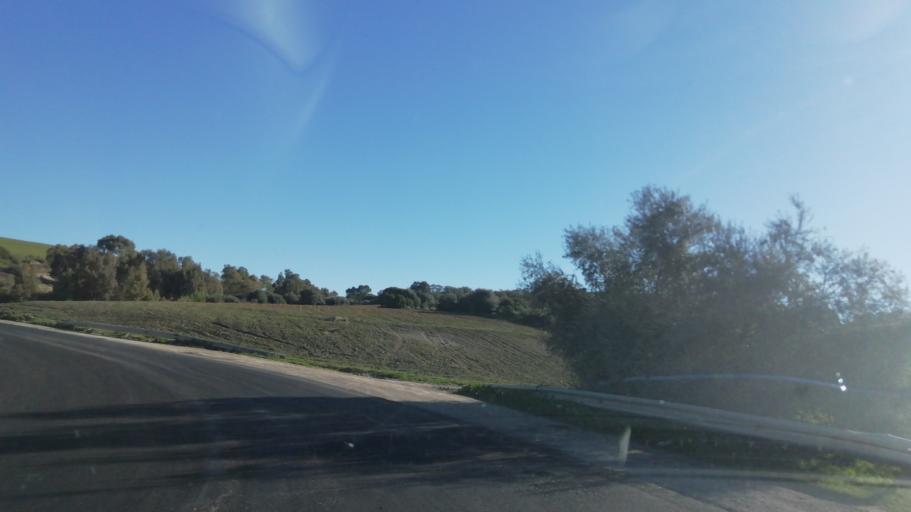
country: DZ
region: Relizane
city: Smala
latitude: 35.6609
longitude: 0.8115
